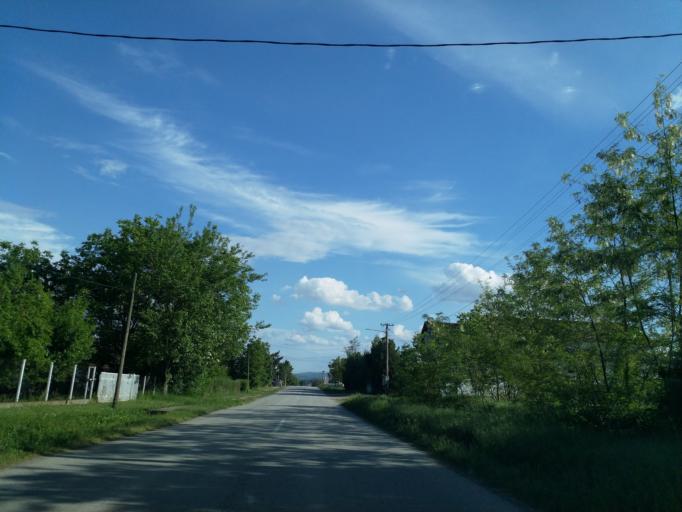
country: RS
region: Central Serbia
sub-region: Sumadijski Okrug
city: Lapovo
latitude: 44.1967
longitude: 21.0892
